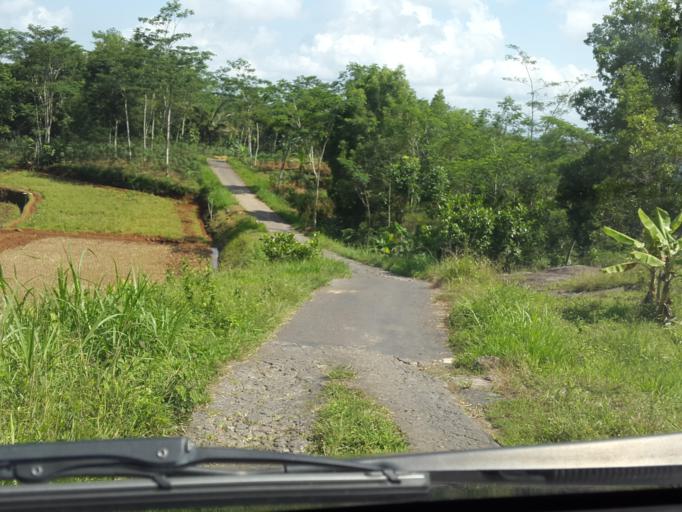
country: ID
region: Central Java
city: Selogiri
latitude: -7.9127
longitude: 110.7698
